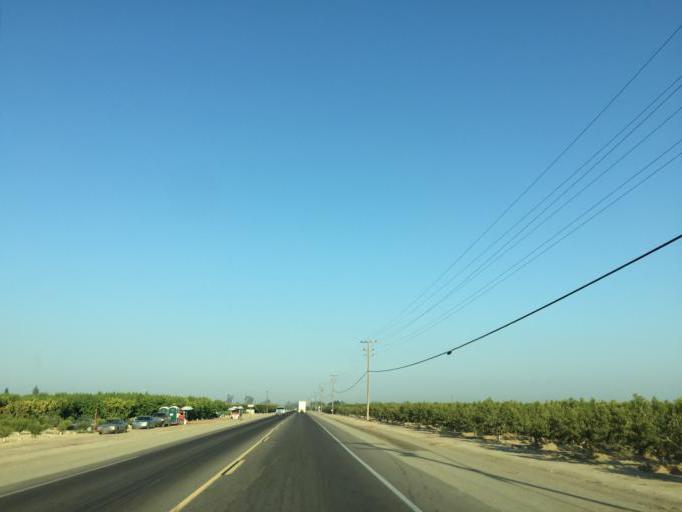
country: US
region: California
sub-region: Tulare County
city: London
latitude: 36.4887
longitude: -119.4938
